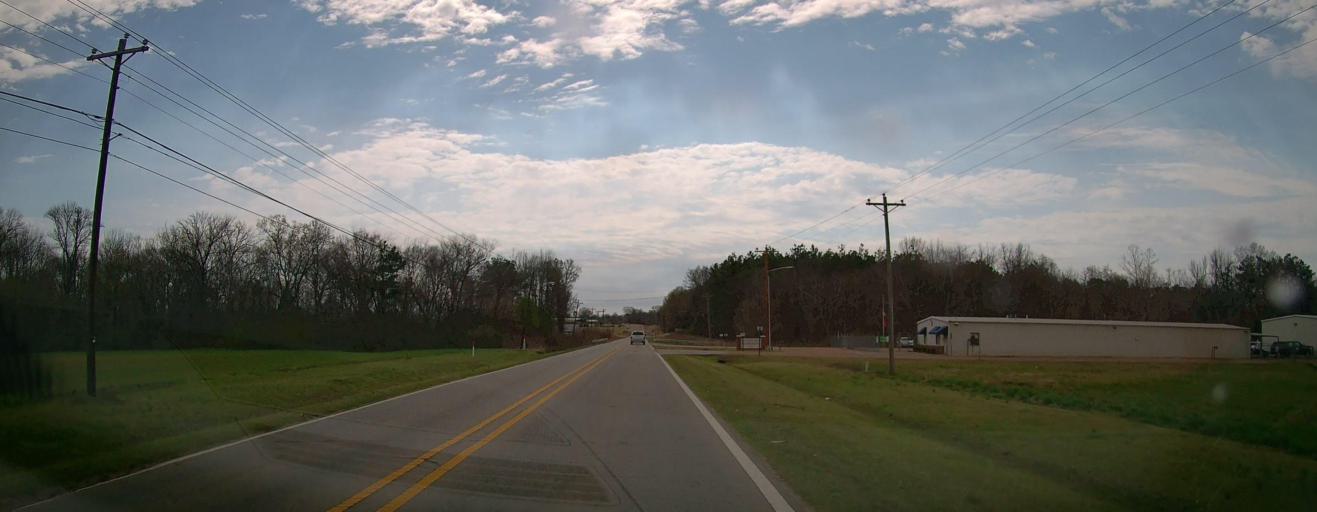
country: US
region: Mississippi
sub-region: De Soto County
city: Olive Branch
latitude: 34.9466
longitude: -89.8094
